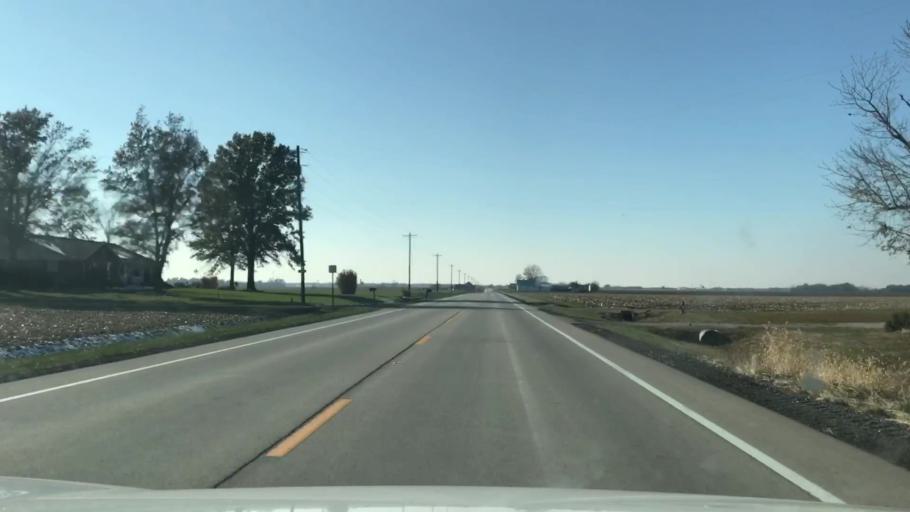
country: US
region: Illinois
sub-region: Washington County
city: Okawville
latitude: 38.4423
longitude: -89.4954
